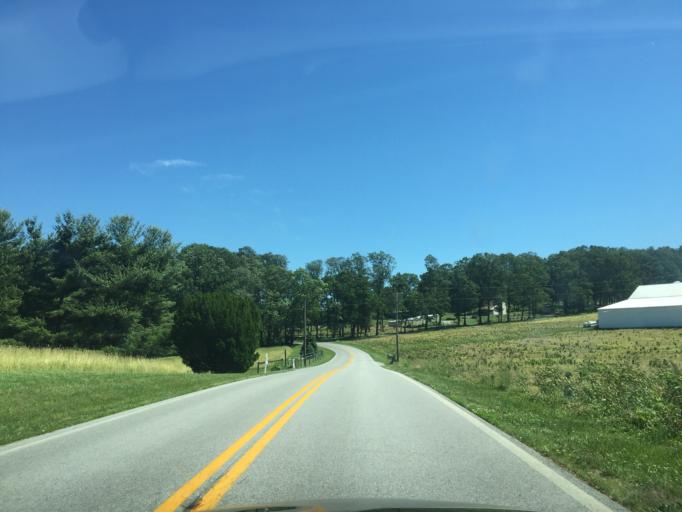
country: US
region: Maryland
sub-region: Carroll County
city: Manchester
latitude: 39.6359
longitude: -76.9174
